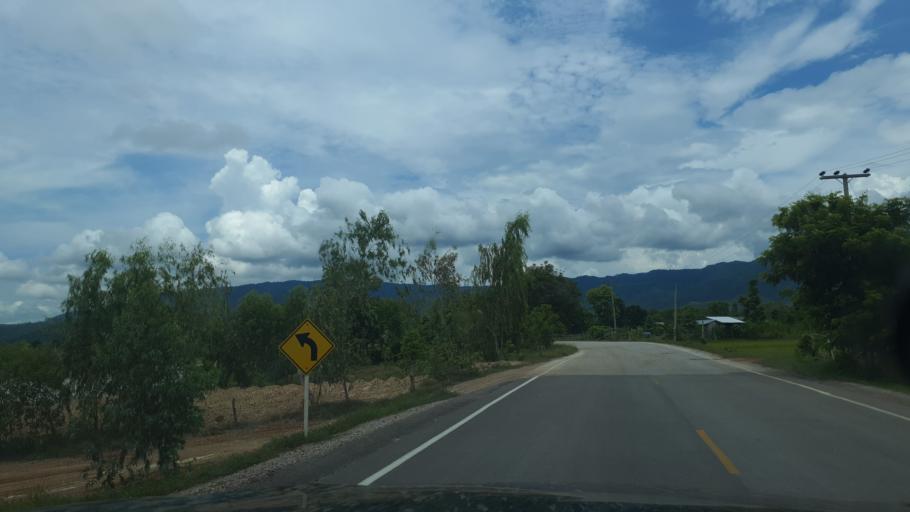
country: TH
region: Lampang
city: Sop Prap
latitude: 17.9141
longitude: 99.3914
